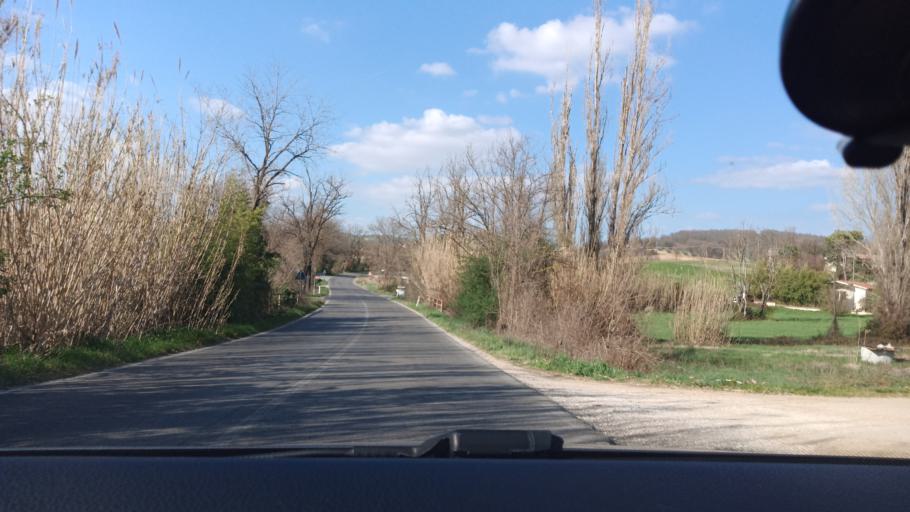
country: IT
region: Latium
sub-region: Citta metropolitana di Roma Capitale
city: Torrita Tiberina
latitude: 42.2580
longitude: 12.6393
